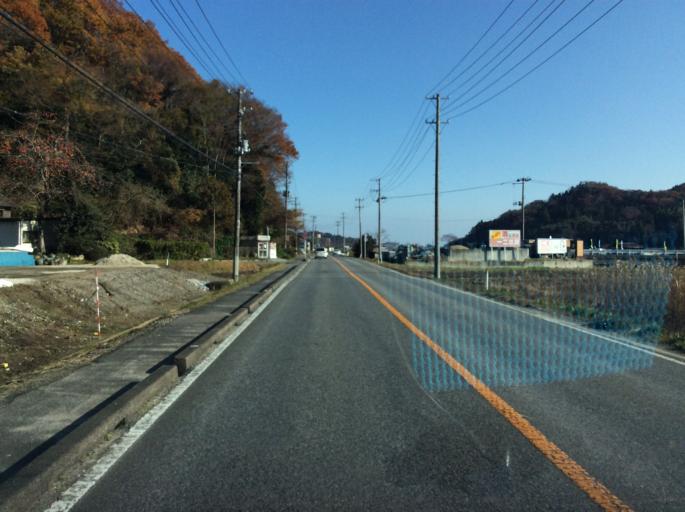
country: JP
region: Fukushima
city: Iwaki
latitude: 37.0341
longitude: 140.9218
